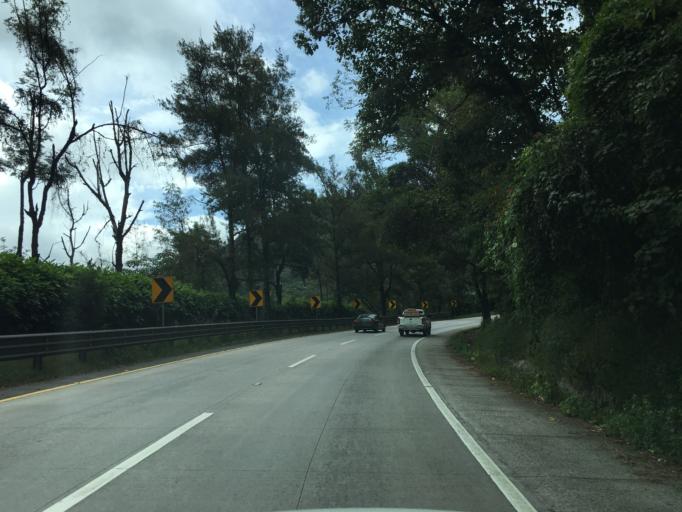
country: GT
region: Sacatepequez
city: Santa Lucia Milpas Altas
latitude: 14.5621
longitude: -90.6992
